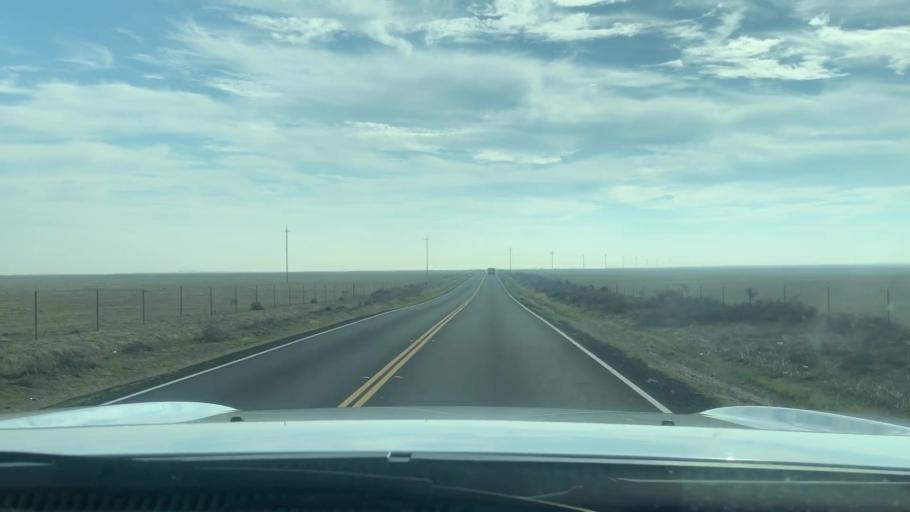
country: US
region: California
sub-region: Kern County
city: Lost Hills
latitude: 35.5926
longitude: -119.8402
